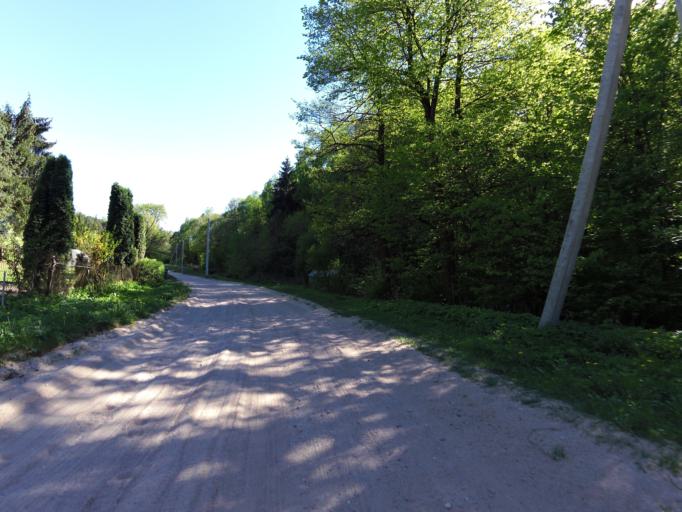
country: LT
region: Vilnius County
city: Pilaite
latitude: 54.6906
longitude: 25.1546
